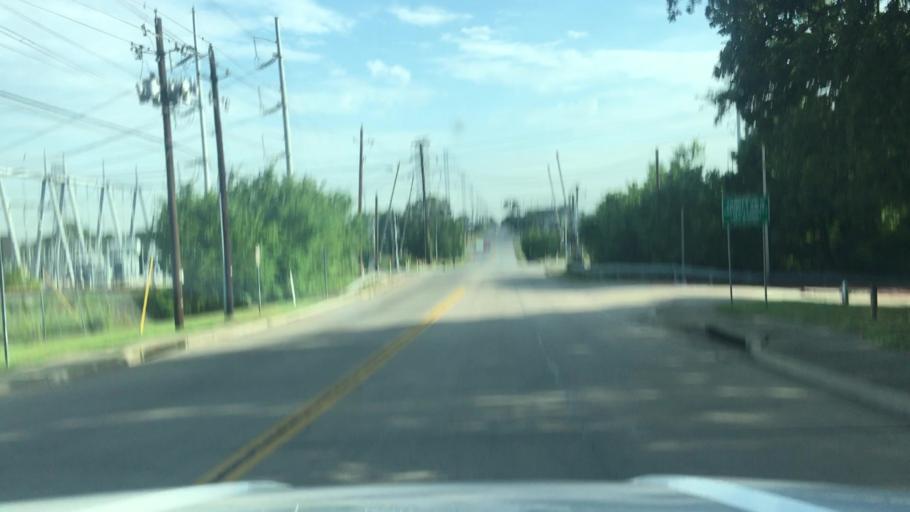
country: US
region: Texas
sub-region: Dallas County
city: Irving
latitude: 32.8136
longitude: -96.9168
